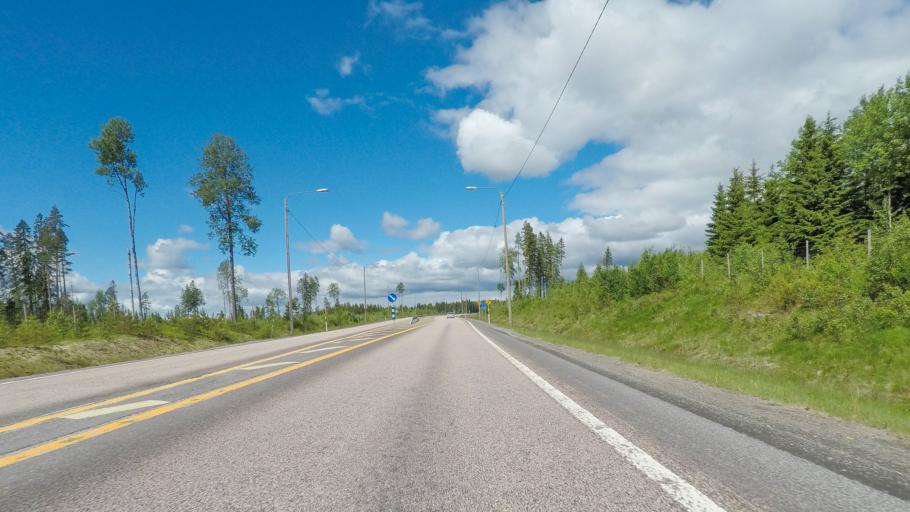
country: FI
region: Paijanne Tavastia
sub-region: Lahti
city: Heinola
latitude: 61.3557
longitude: 26.0431
